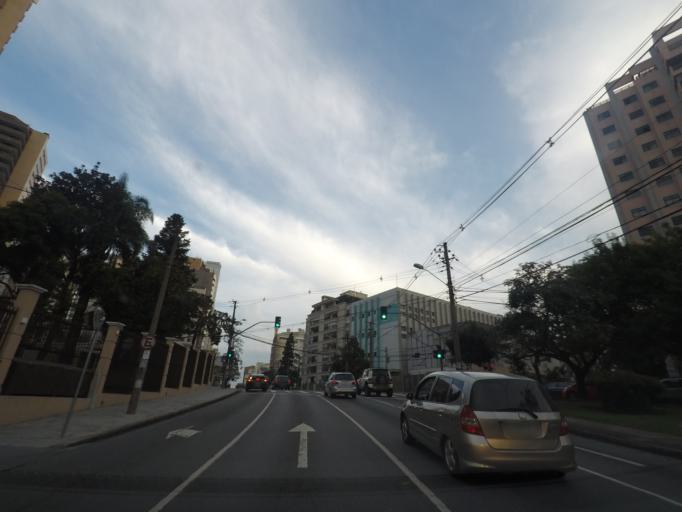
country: BR
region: Parana
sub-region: Curitiba
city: Curitiba
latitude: -25.4075
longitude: -49.2563
